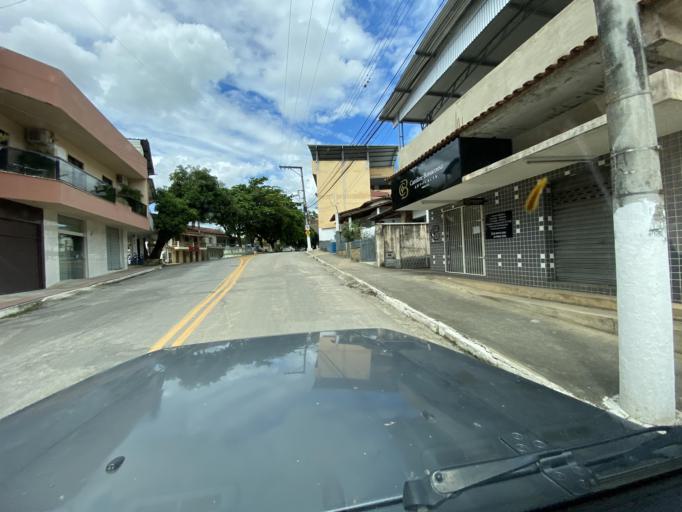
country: BR
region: Espirito Santo
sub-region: Jeronimo Monteiro
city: Jeronimo Monteiro
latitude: -20.7892
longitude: -41.3956
